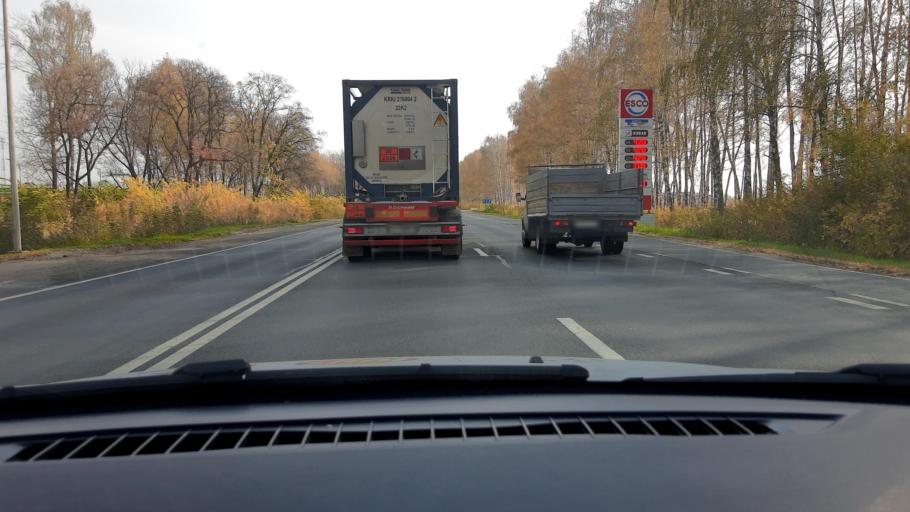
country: RU
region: Nizjnij Novgorod
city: Pamyat' Parizhskoy Kommuny
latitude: 56.0612
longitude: 44.3867
